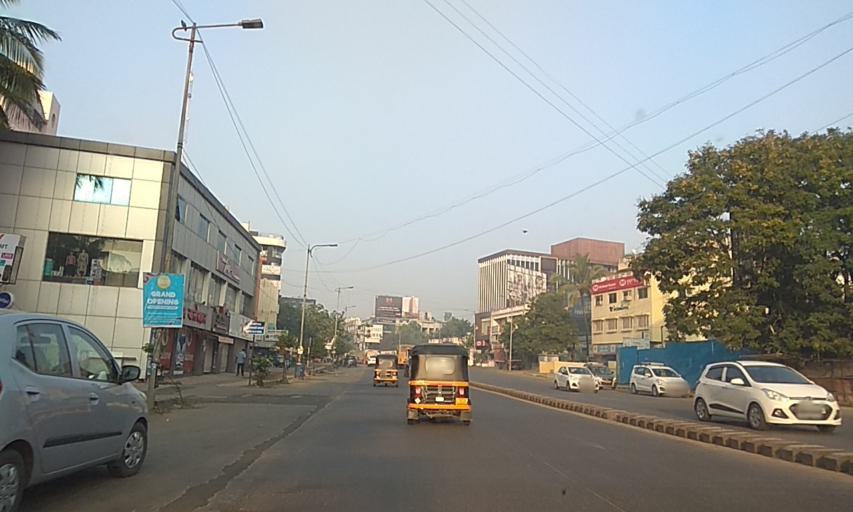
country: IN
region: Maharashtra
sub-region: Pune Division
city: Pimpri
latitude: 18.5637
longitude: 73.7823
